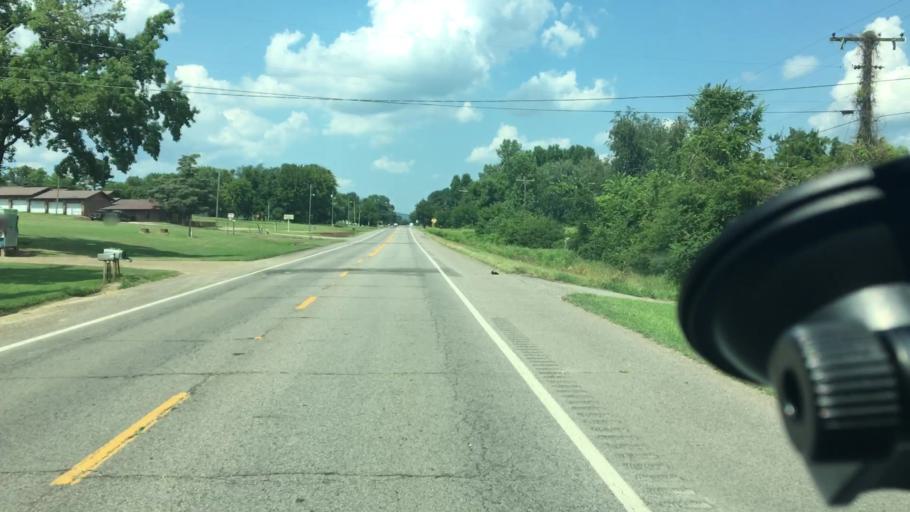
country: US
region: Arkansas
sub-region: Logan County
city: Paris
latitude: 35.2940
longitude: -93.6956
